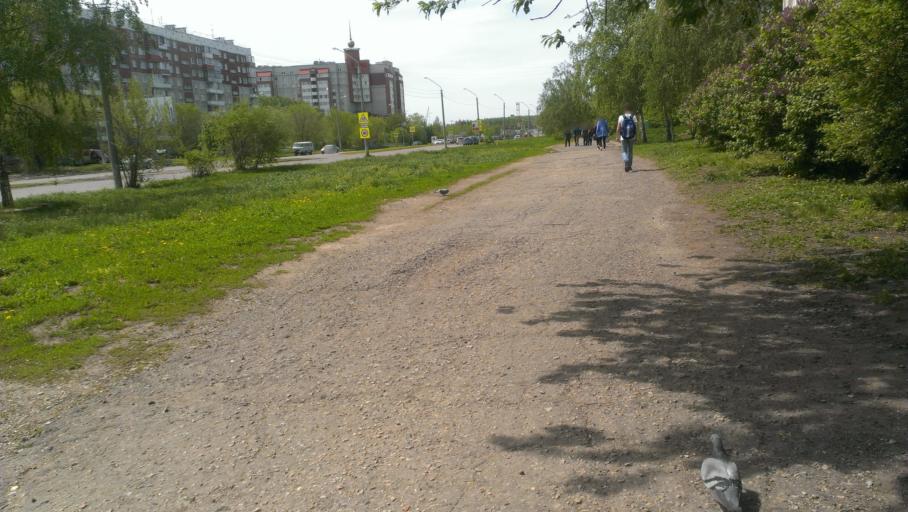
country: RU
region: Altai Krai
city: Novosilikatnyy
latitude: 53.3626
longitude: 83.6712
